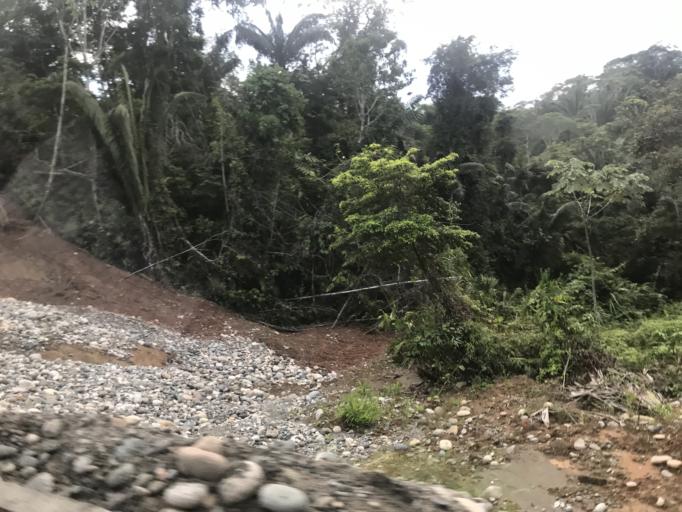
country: EC
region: Napo
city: Tena
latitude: -1.0643
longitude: -77.7010
